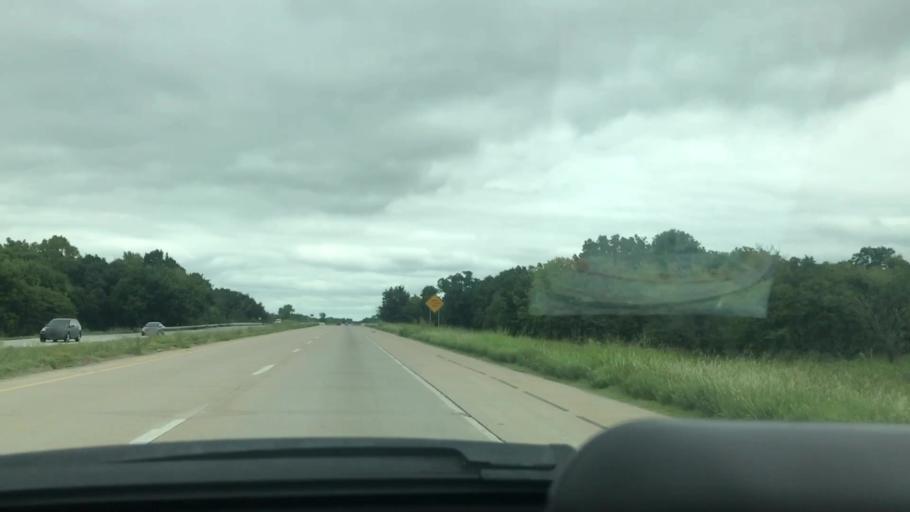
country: US
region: Oklahoma
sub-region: Mayes County
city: Chouteau
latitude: 36.2047
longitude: -95.3407
